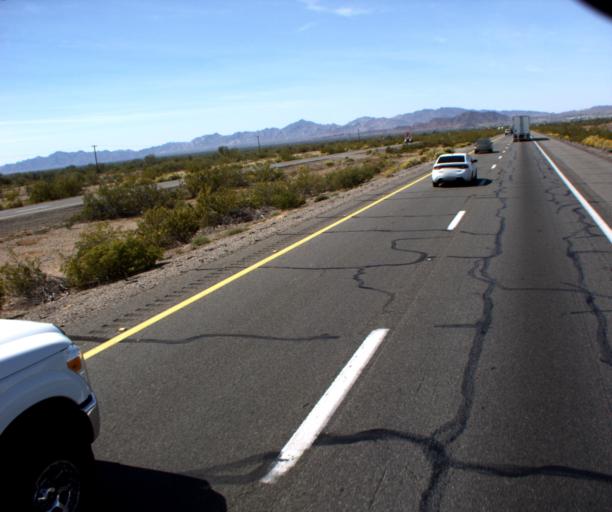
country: US
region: Arizona
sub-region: La Paz County
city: Quartzsite
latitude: 33.6721
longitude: -114.1492
